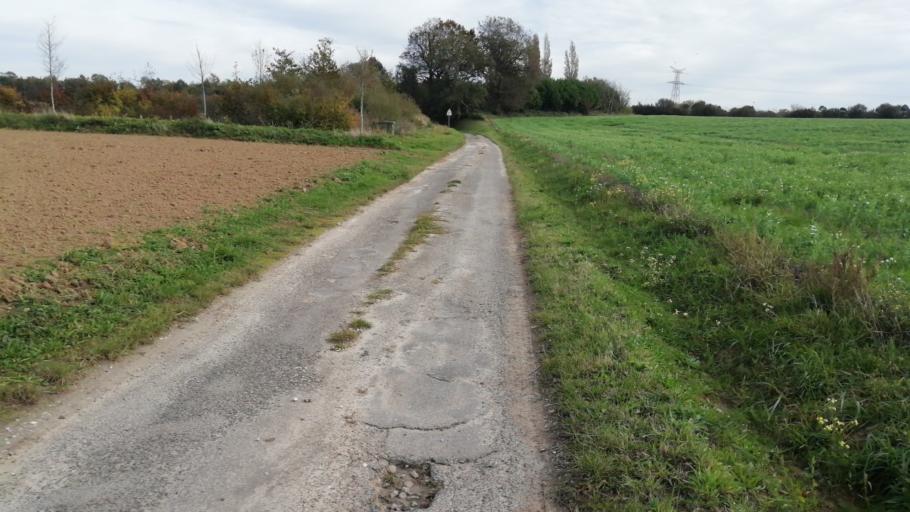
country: FR
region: Haute-Normandie
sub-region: Departement de la Seine-Maritime
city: Epouville
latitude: 49.5484
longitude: 0.2307
